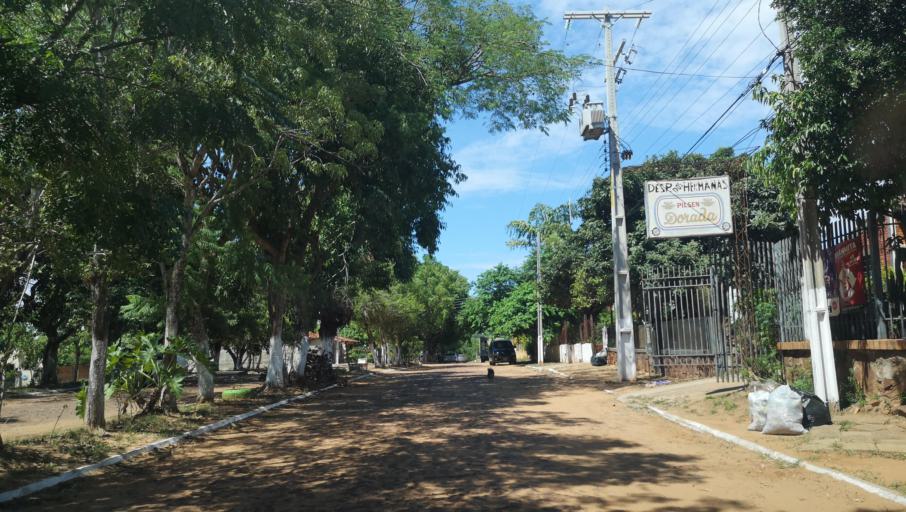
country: PY
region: Misiones
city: Santa Maria
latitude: -26.8793
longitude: -57.0249
